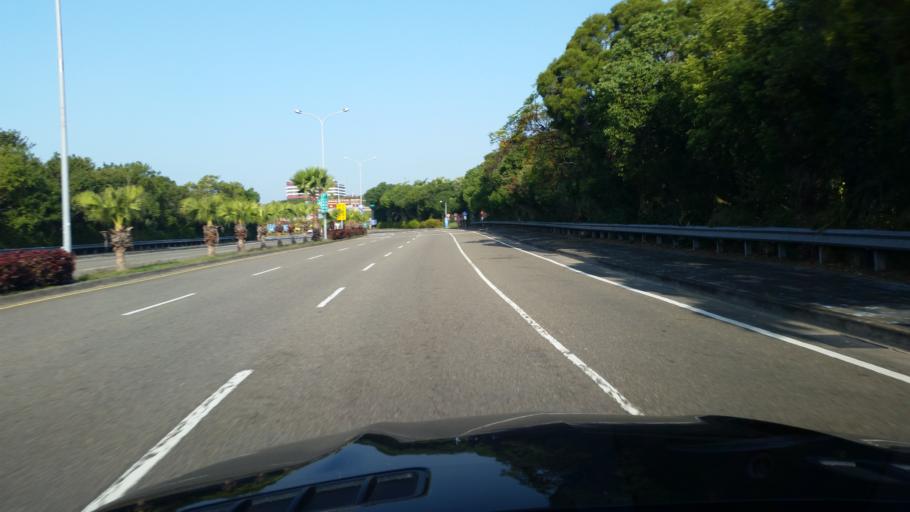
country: TW
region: Taiwan
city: Fengyuan
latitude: 24.3167
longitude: 120.6954
